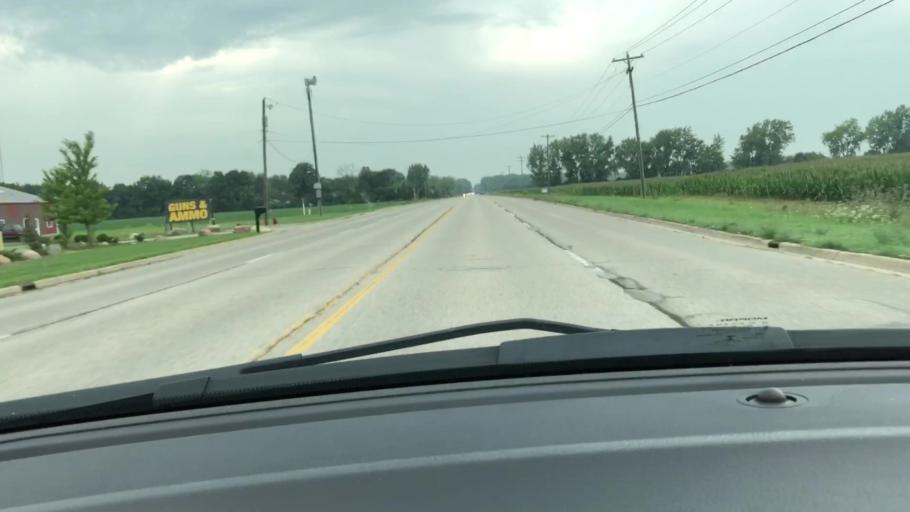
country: US
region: Michigan
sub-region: Saginaw County
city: Freeland
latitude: 43.4812
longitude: -84.0770
